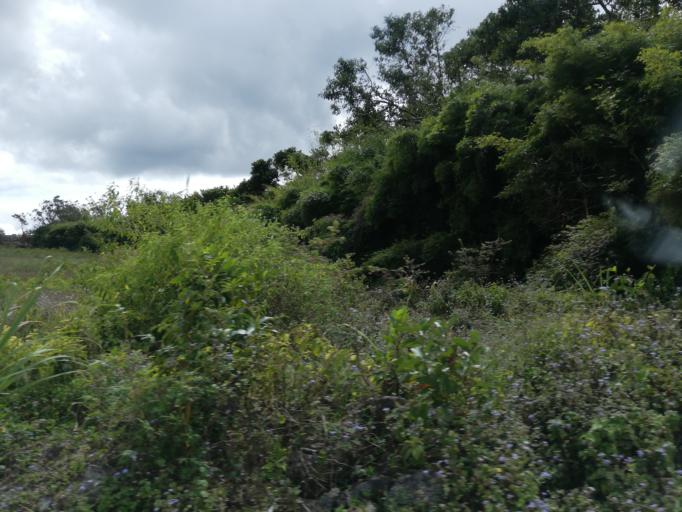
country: MU
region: Moka
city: Camp Thorel
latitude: -20.2138
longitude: 57.5982
